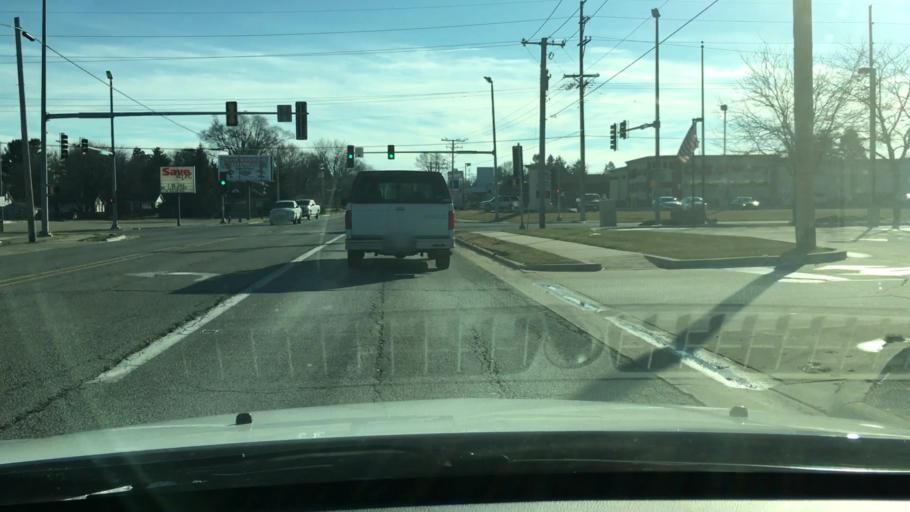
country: US
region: Illinois
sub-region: LaSalle County
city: Mendota
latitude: 41.5559
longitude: -89.1278
